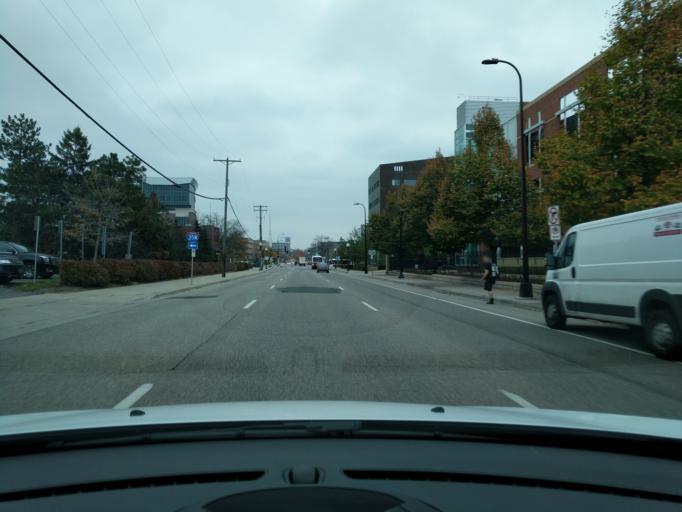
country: US
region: Minnesota
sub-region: Ramsey County
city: Lauderdale
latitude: 44.9764
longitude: -93.2287
